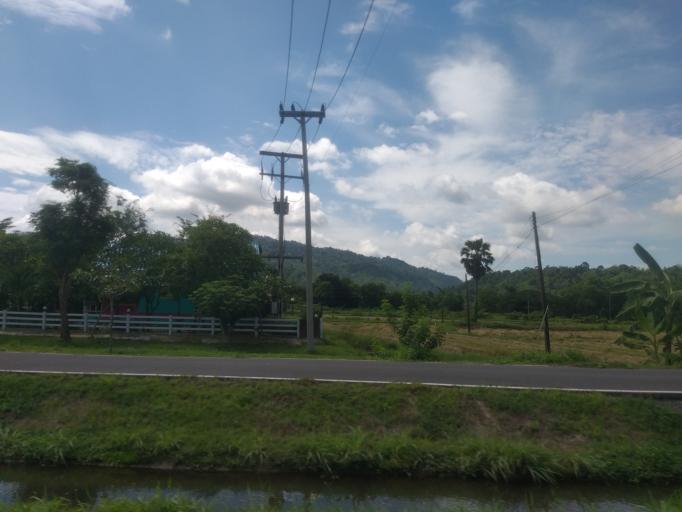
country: TH
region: Nakhon Nayok
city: Nakhon Nayok
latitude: 14.3021
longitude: 101.3082
